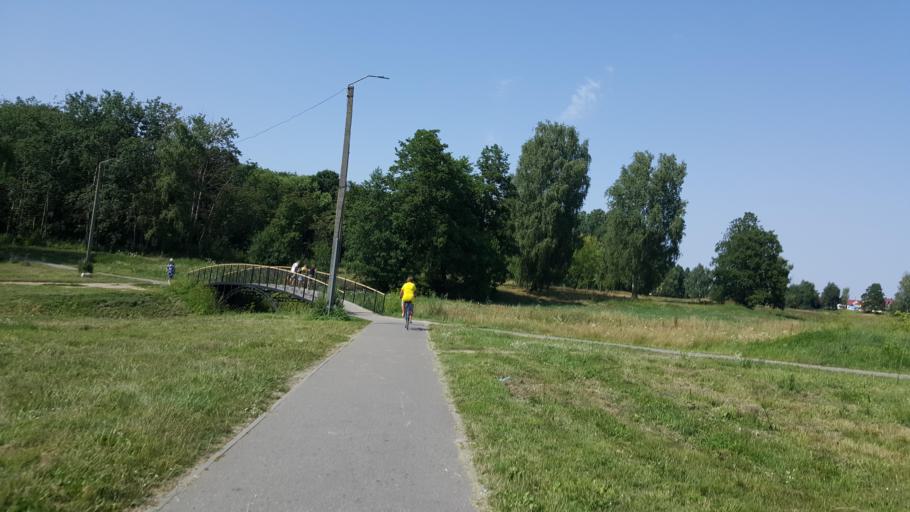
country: BY
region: Brest
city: Zhabinka
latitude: 52.1939
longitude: 24.0295
